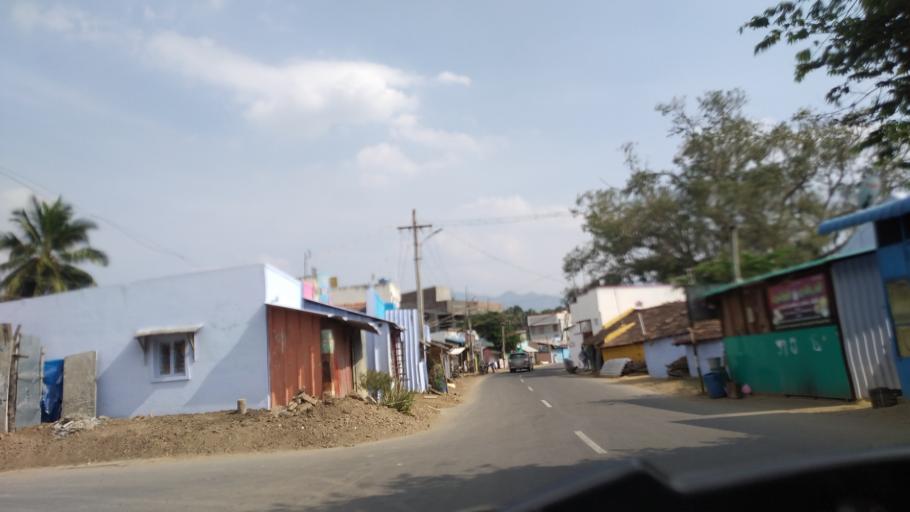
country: IN
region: Tamil Nadu
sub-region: Coimbatore
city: Perur
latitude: 10.9575
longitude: 76.7592
